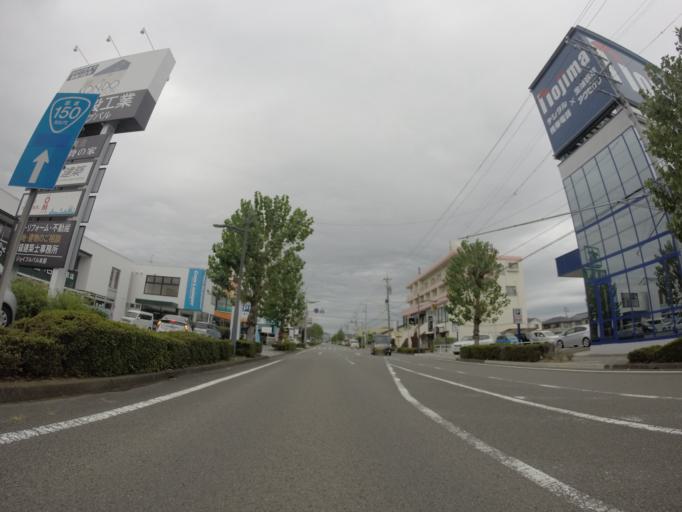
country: JP
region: Shizuoka
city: Yaizu
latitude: 34.8596
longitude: 138.3114
